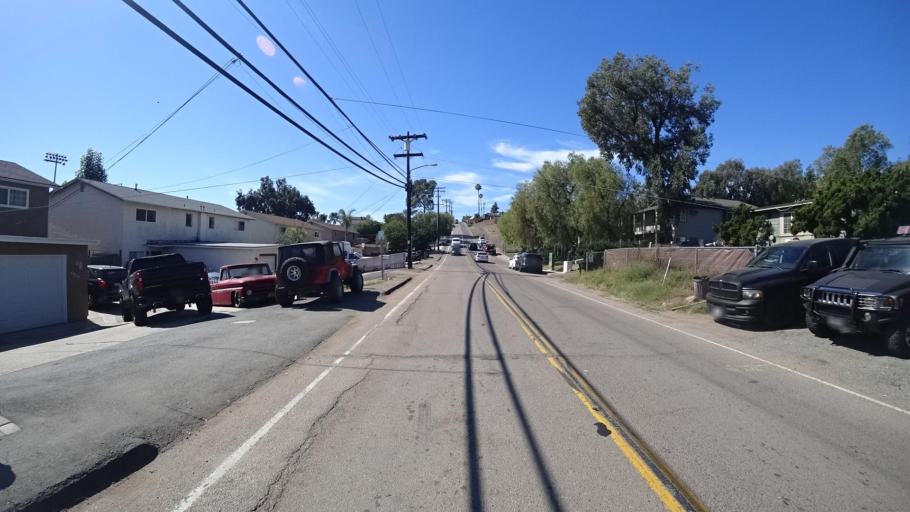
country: US
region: California
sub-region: San Diego County
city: La Presa
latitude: 32.7190
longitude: -117.0059
